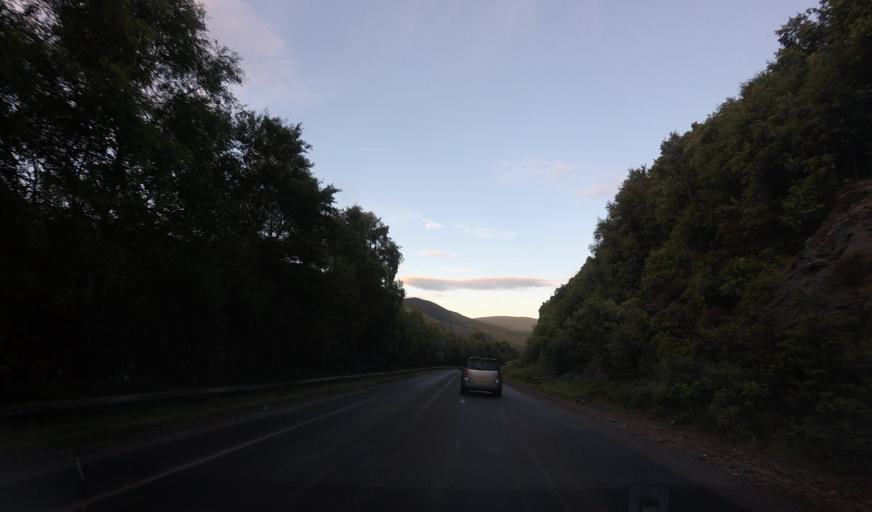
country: GB
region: Scotland
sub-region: Argyll and Bute
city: Helensburgh
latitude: 56.1680
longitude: -4.6729
